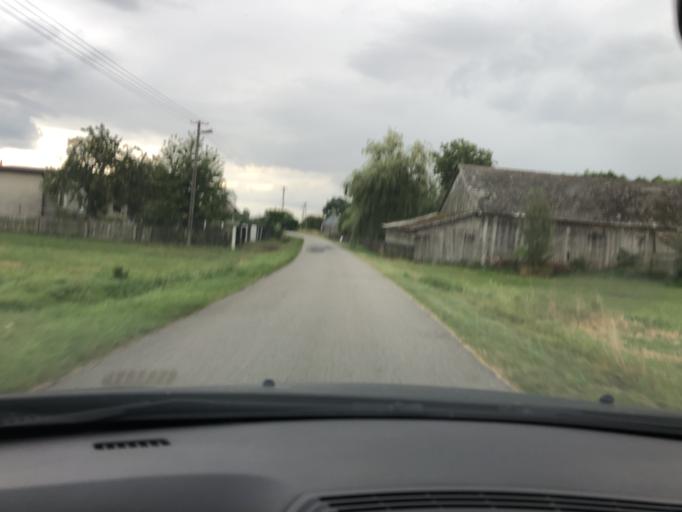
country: PL
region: Lodz Voivodeship
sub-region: Powiat wieruszowski
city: Czastary
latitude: 51.2420
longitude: 18.2809
